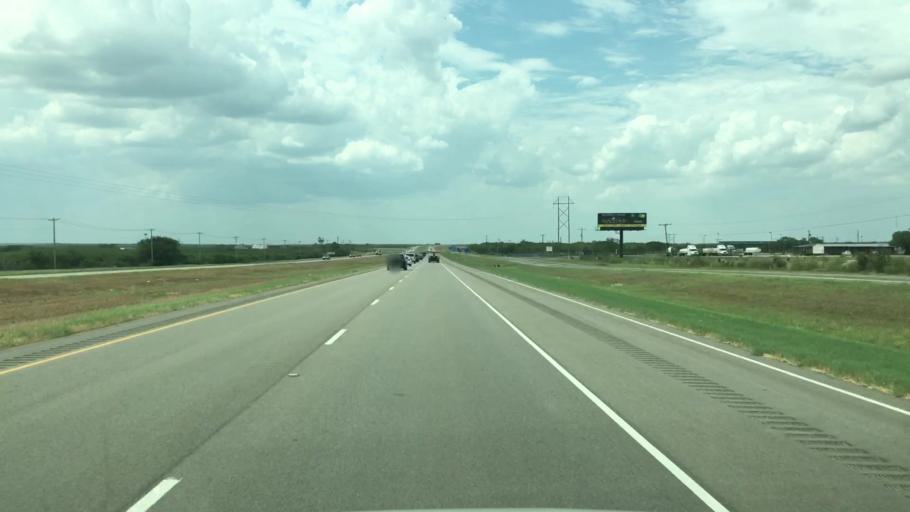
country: US
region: Texas
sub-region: Live Oak County
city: Three Rivers
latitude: 28.5120
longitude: -98.1700
